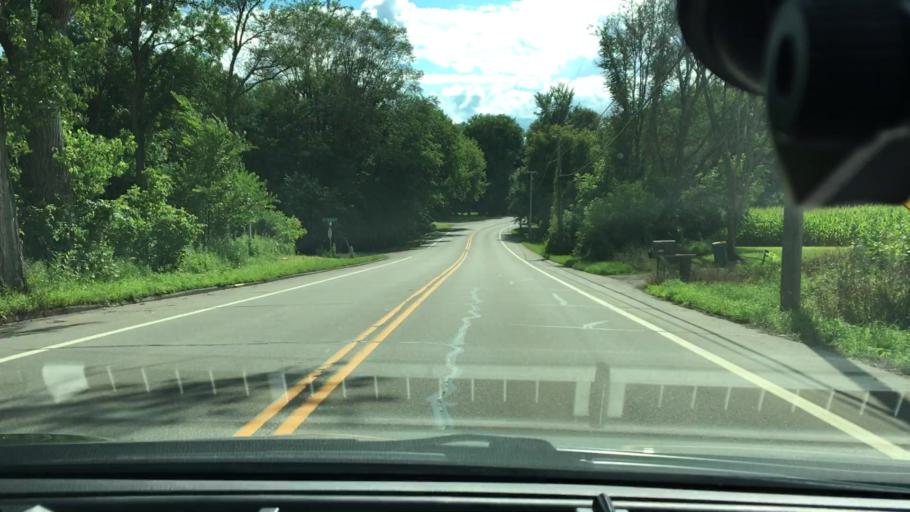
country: US
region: Minnesota
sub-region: Hennepin County
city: Minnetrista
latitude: 44.9229
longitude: -93.6945
